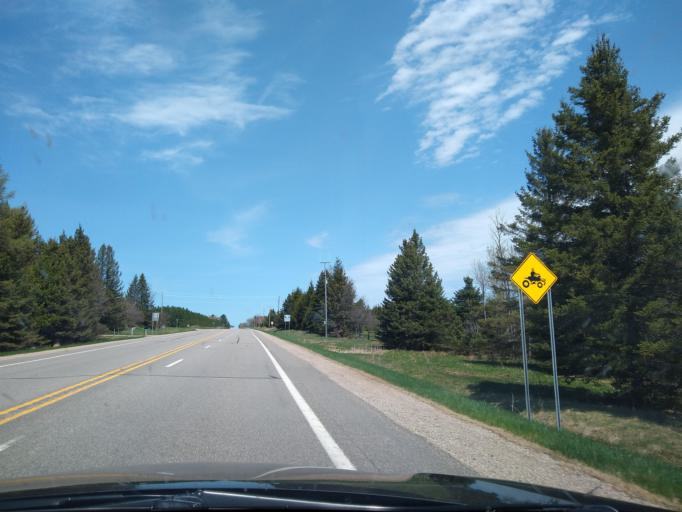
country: US
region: Michigan
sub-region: Delta County
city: Gladstone
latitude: 46.0769
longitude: -86.9809
